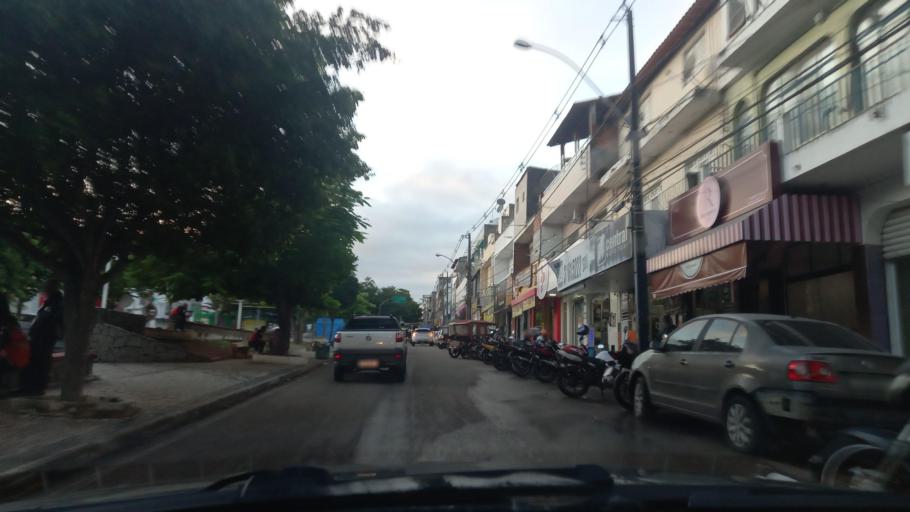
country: BR
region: Bahia
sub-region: Paulo Afonso
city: Paulo Afonso
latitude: -9.4031
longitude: -38.2163
